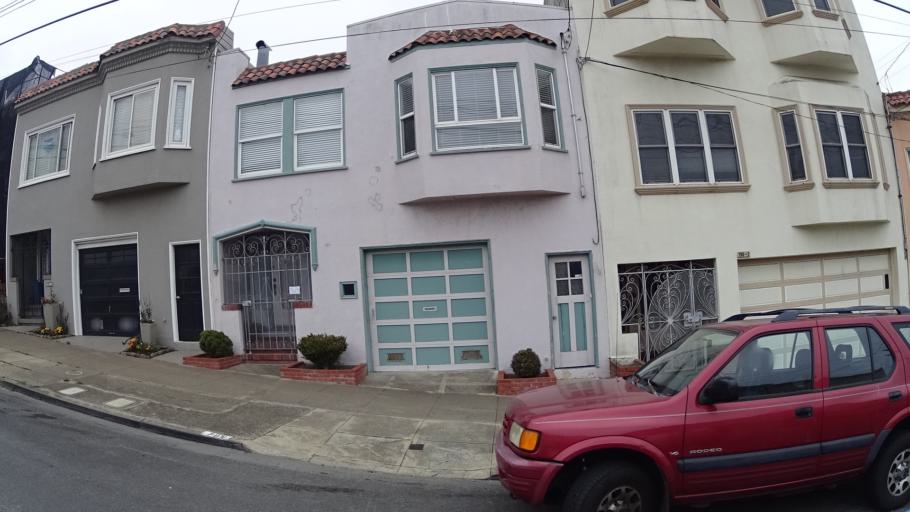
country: US
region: California
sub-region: San Francisco County
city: San Francisco
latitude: 37.7742
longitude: -122.4940
